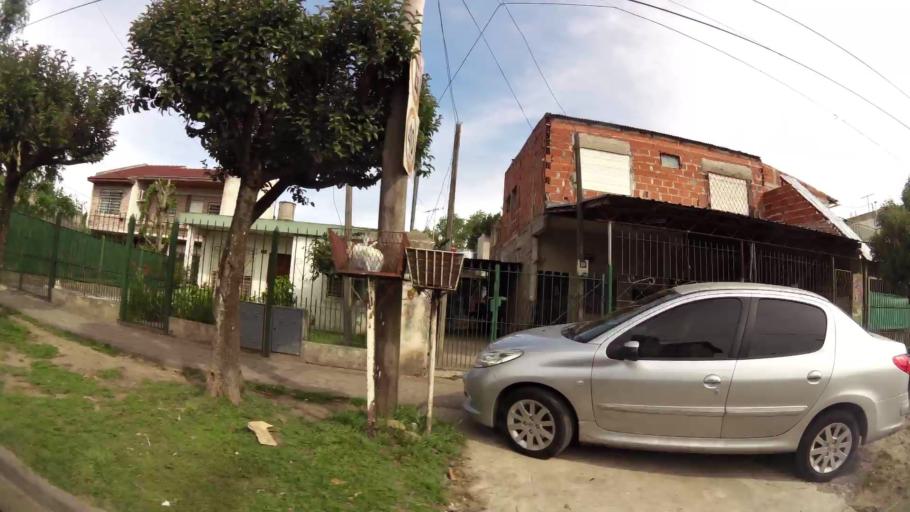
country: AR
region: Buenos Aires
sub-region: Partido de Quilmes
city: Quilmes
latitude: -34.7672
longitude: -58.2548
